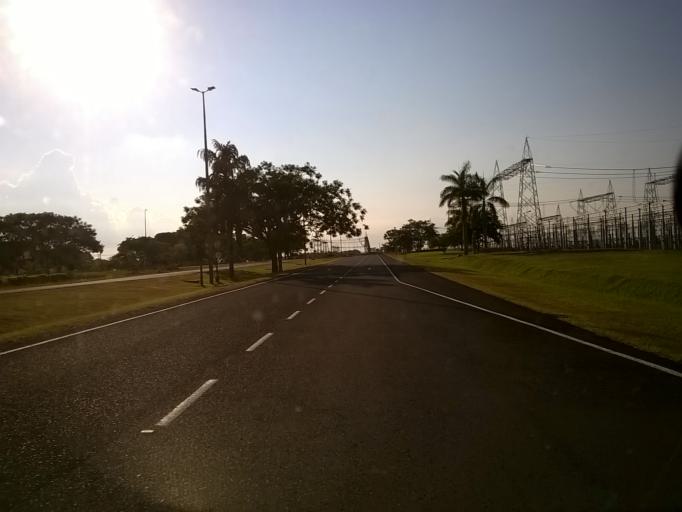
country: PY
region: Alto Parana
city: Ciudad del Este
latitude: -25.4153
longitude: -54.6131
